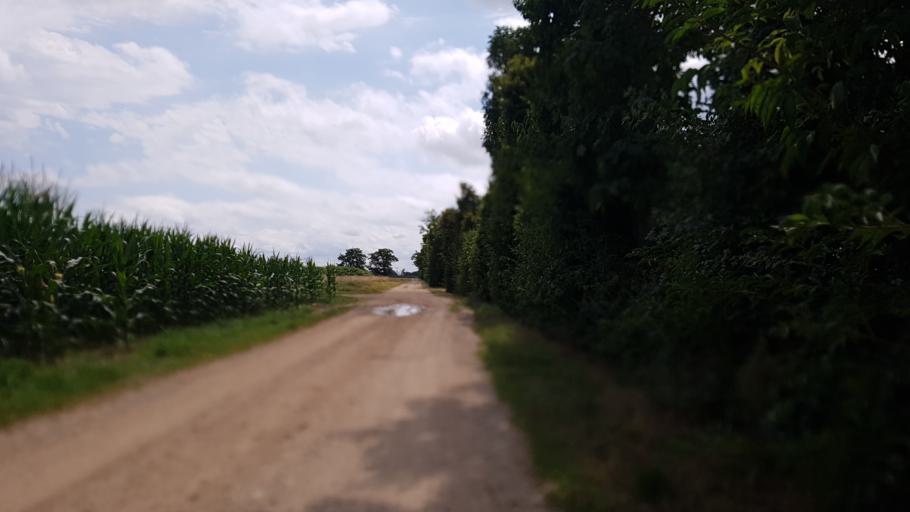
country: FR
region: Rhone-Alpes
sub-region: Departement du Rhone
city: Pusignan
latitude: 45.7270
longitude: 5.0498
